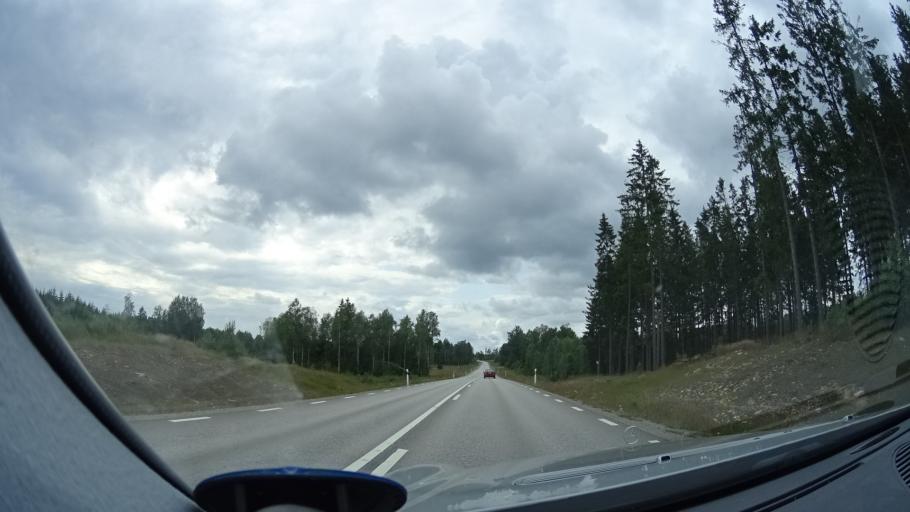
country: SE
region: Kronoberg
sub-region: Tingsryds Kommun
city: Tingsryd
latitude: 56.5048
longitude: 15.0333
